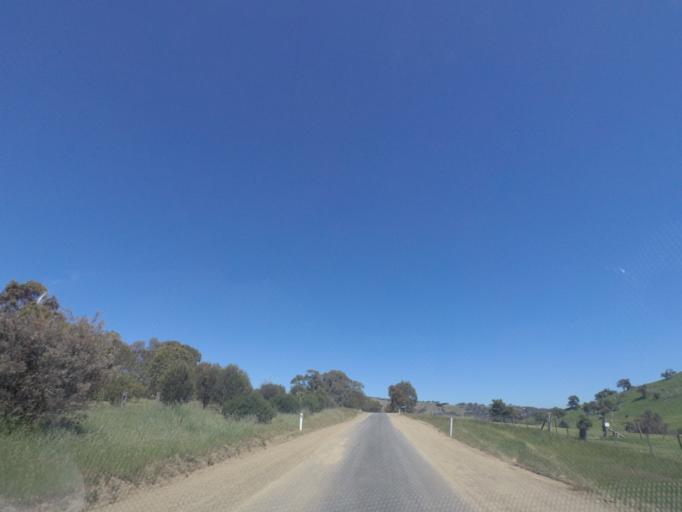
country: AU
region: Victoria
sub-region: Whittlesea
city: Whittlesea
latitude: -37.2881
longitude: 144.9958
